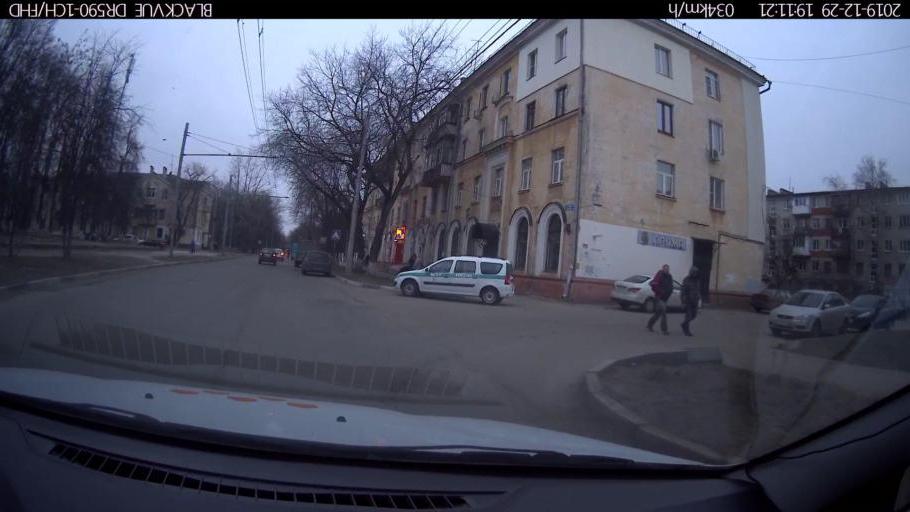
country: RU
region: Nizjnij Novgorod
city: Nizhniy Novgorod
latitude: 56.3303
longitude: 43.8793
